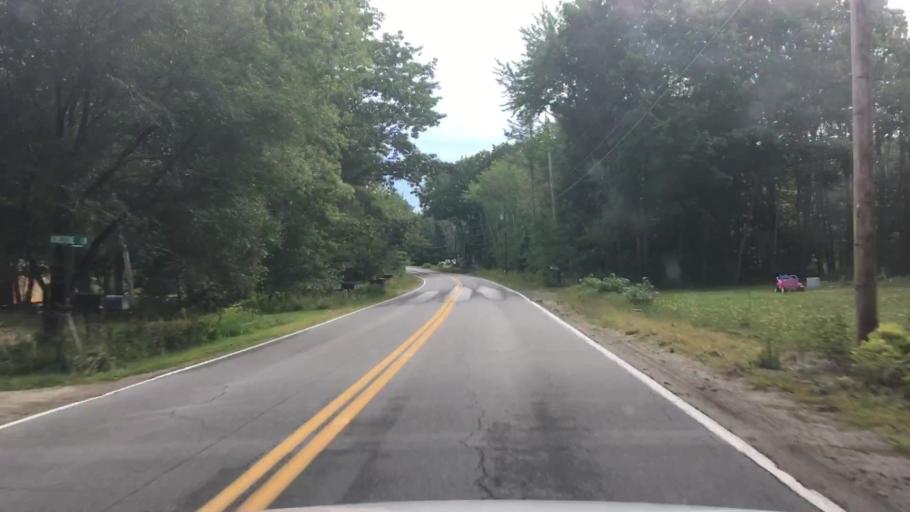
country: US
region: Maine
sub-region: Hancock County
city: Trenton
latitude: 44.4660
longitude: -68.4237
